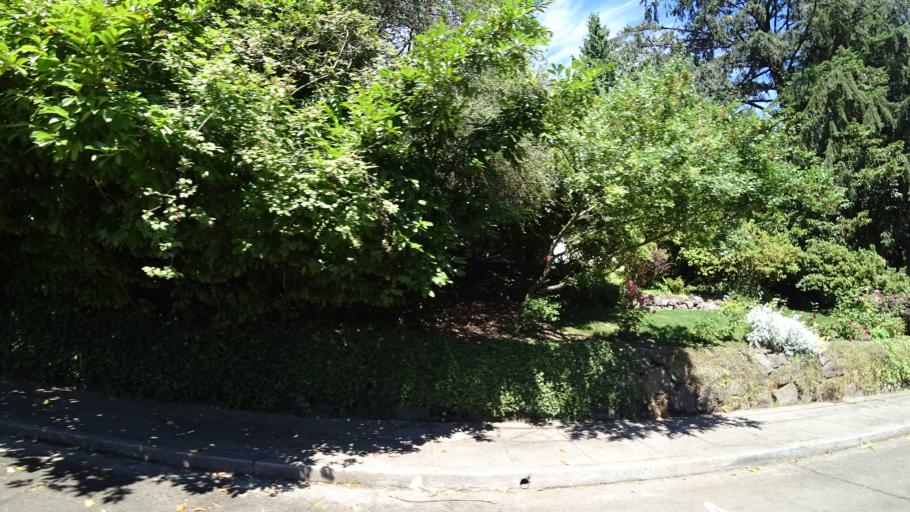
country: US
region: Oregon
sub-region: Multnomah County
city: Portland
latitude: 45.5030
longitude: -122.7022
